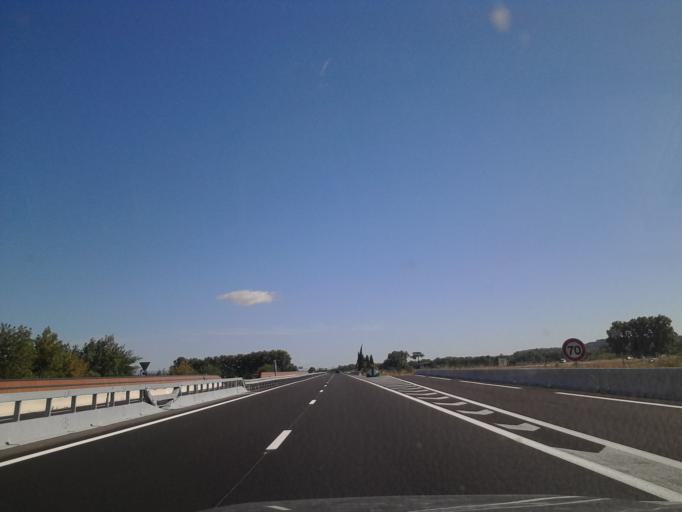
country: FR
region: Languedoc-Roussillon
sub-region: Departement de l'Herault
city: Pezenas
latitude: 43.4501
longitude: 3.4283
